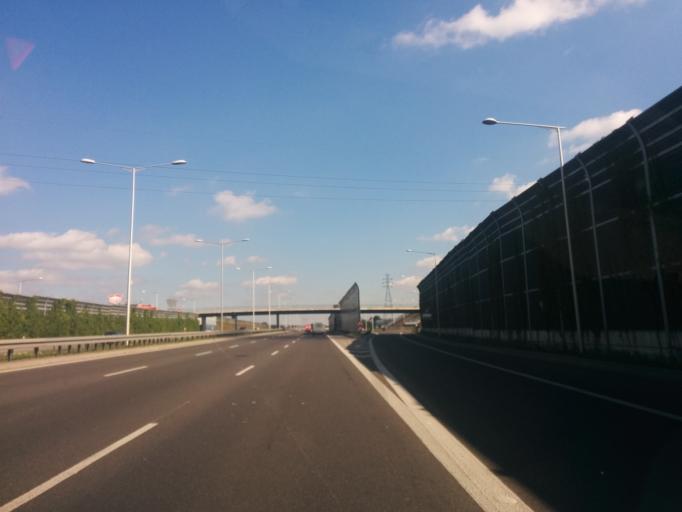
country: PL
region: Masovian Voivodeship
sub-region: Warszawa
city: Targowek
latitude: 52.3036
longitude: 21.0490
